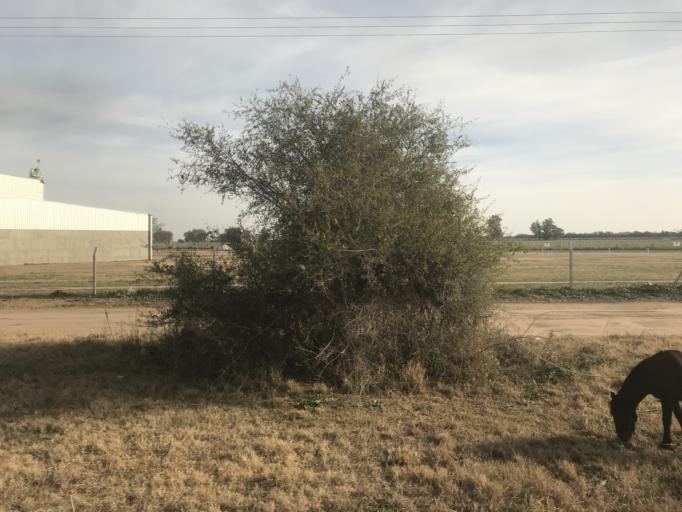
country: AR
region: Cordoba
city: Pilar
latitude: -31.6714
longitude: -63.8952
